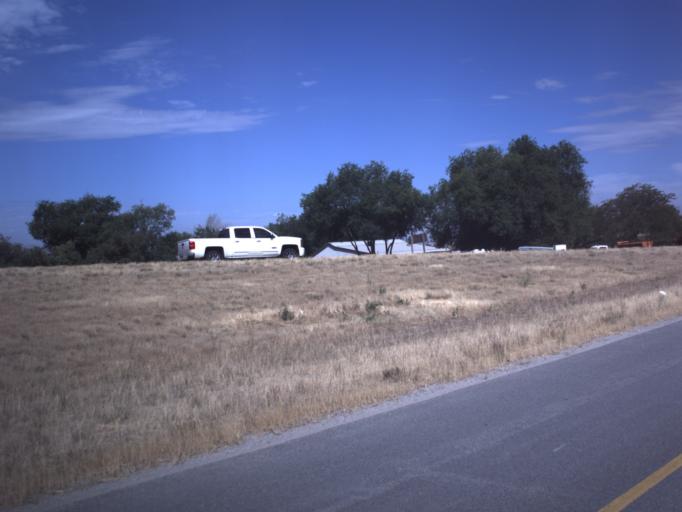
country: US
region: Utah
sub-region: Box Elder County
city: South Willard
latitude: 41.3454
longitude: -112.0328
